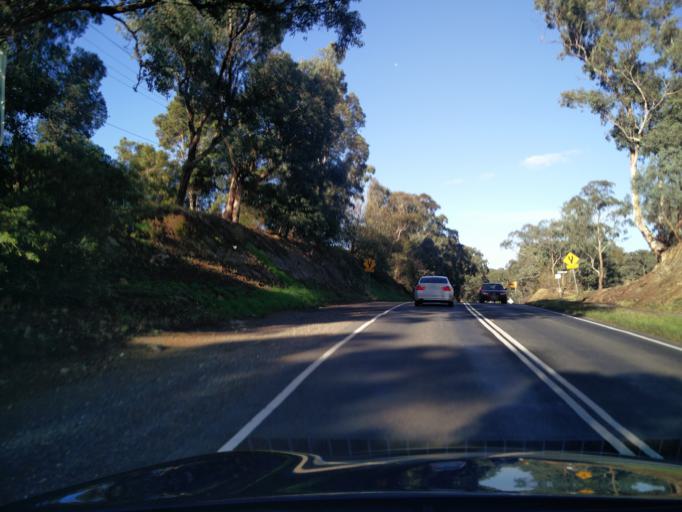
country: AU
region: Victoria
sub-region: Nillumbik
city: North Warrandyte
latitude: -37.7451
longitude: 145.2108
